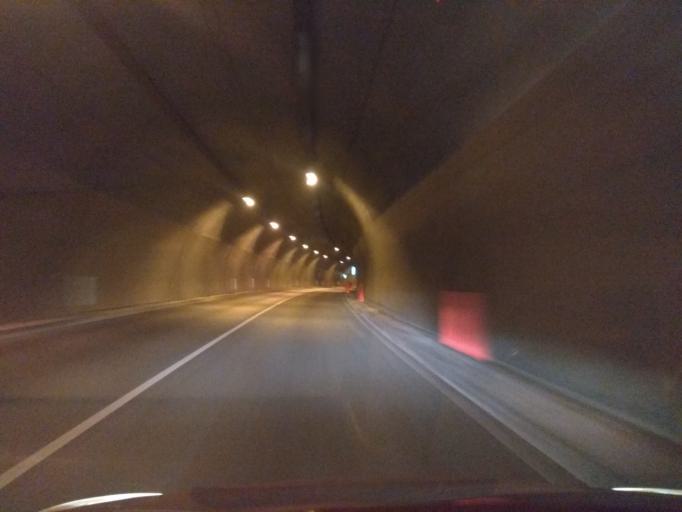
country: IT
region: Piedmont
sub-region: Provincia di Biella
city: Vallanzengo
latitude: 45.6156
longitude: 8.1521
